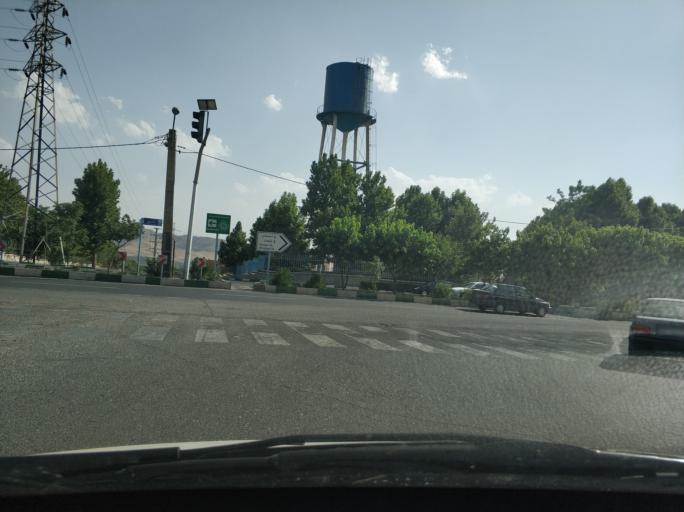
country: IR
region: Tehran
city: Tajrish
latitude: 35.7452
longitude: 51.5763
